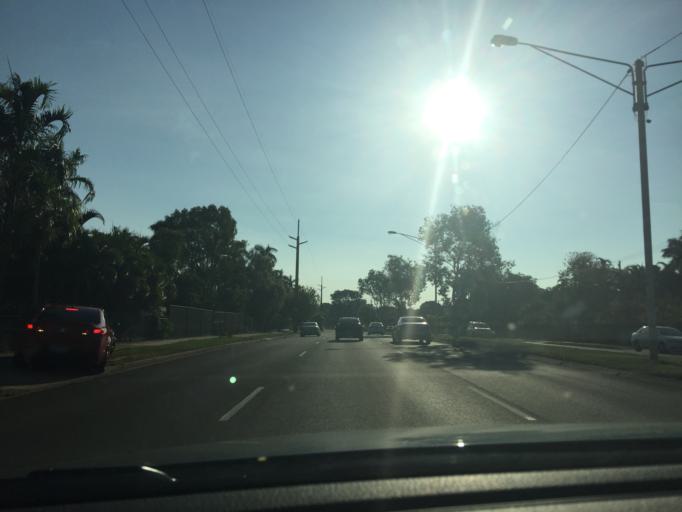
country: AU
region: Northern Territory
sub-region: Darwin
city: Nightcliff
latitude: -12.3834
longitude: 130.8723
